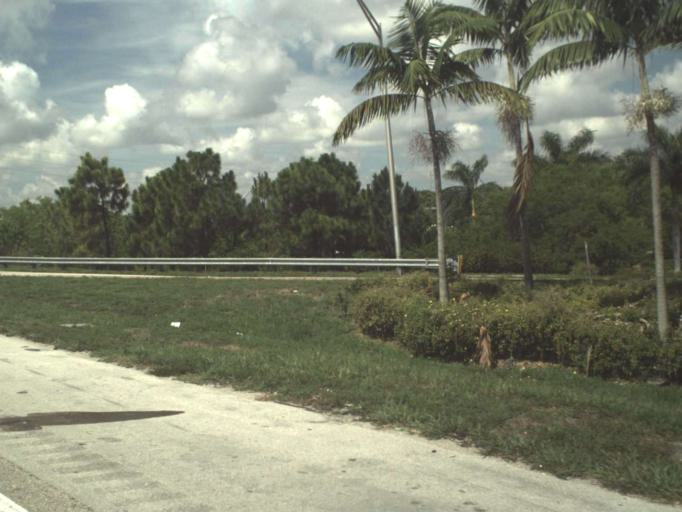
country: US
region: Florida
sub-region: Broward County
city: Twin Lakes
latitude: 26.1675
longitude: -80.1595
